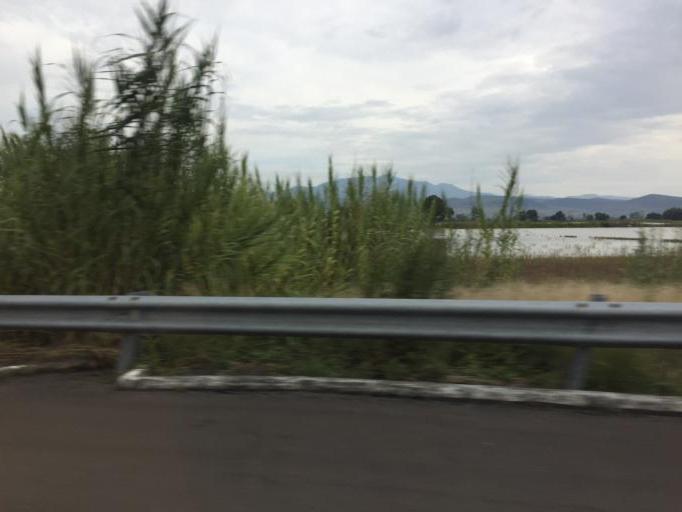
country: MX
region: Mexico
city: Huaniqueo de Morales
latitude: 19.8936
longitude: -101.5442
